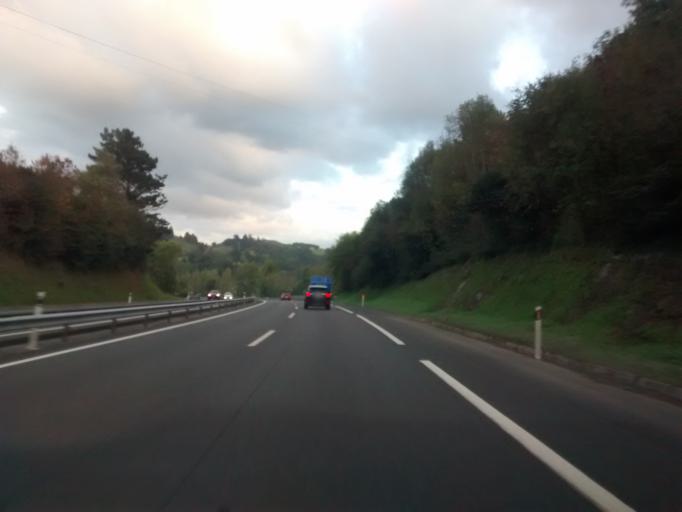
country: ES
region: Basque Country
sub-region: Provincia de Guipuzcoa
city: Zarautz
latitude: 43.2800
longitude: -2.1766
